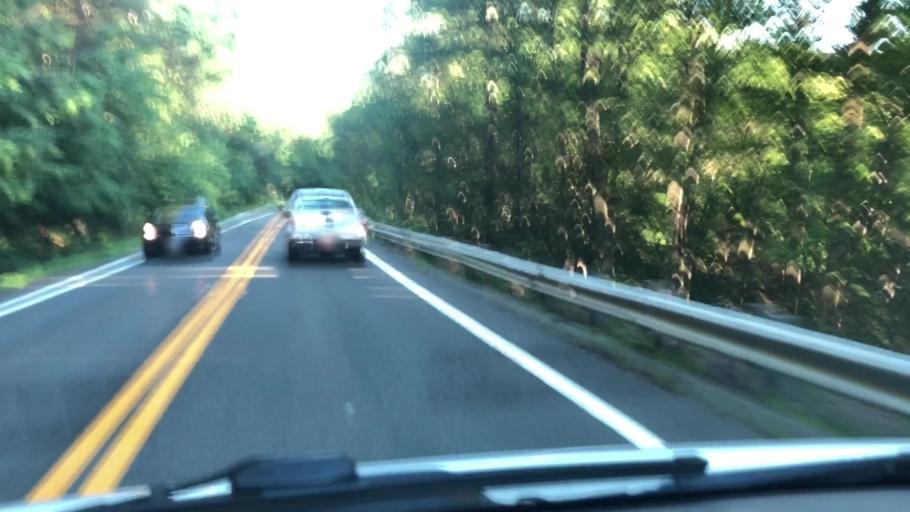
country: US
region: Massachusetts
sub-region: Hampshire County
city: Chesterfield
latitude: 42.3161
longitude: -72.8672
